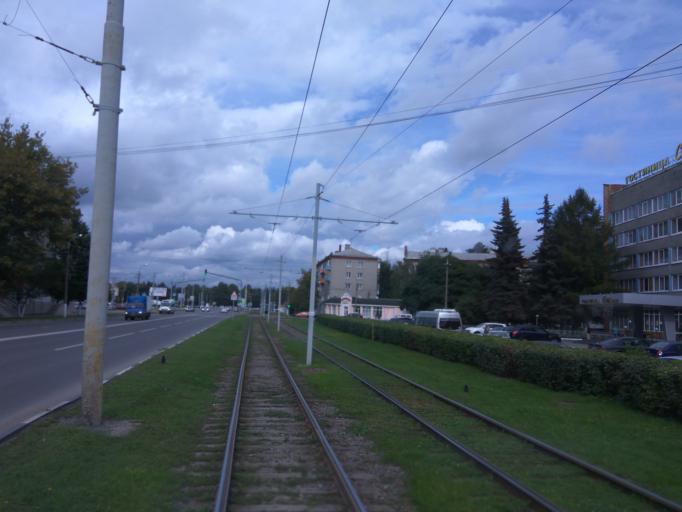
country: RU
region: Moskovskaya
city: Kolomna
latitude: 55.0908
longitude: 38.7672
